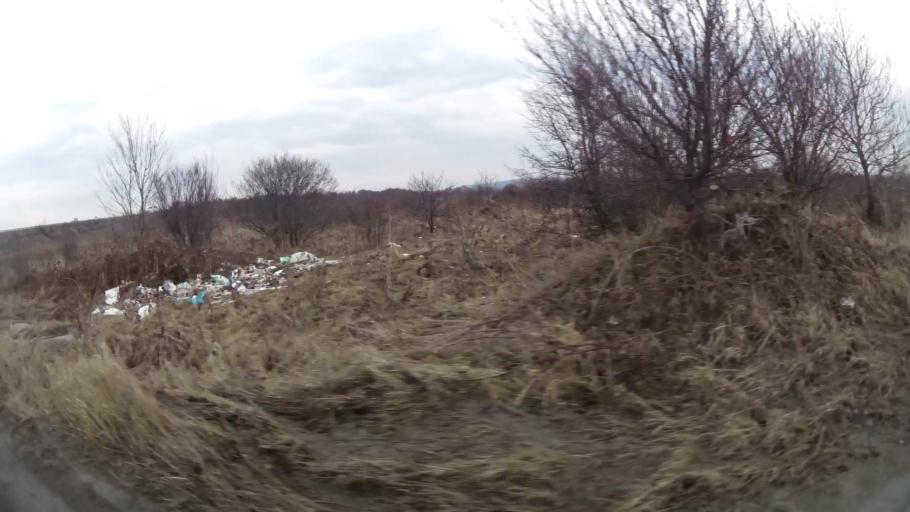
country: BG
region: Sofiya
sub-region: Obshtina Bozhurishte
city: Bozhurishte
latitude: 42.7085
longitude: 23.2189
